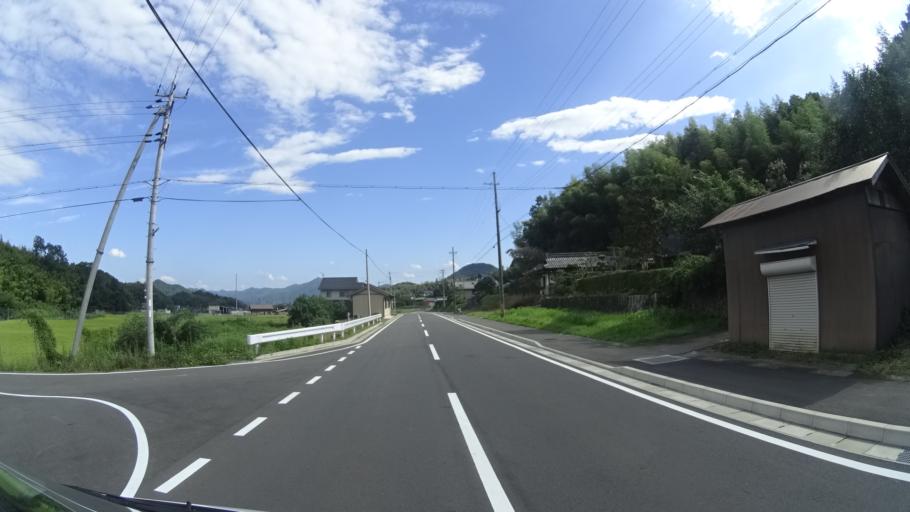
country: JP
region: Kyoto
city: Fukuchiyama
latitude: 35.3333
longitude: 135.1715
